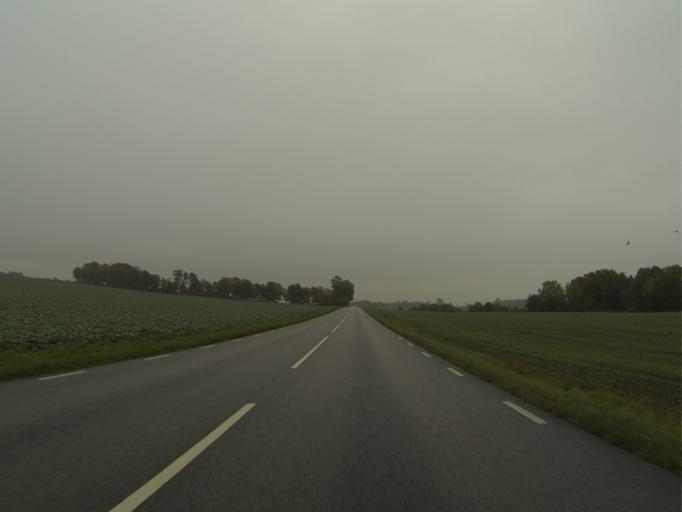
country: SE
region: Skane
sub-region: Hoors Kommun
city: Loberod
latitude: 55.7119
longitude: 13.5431
